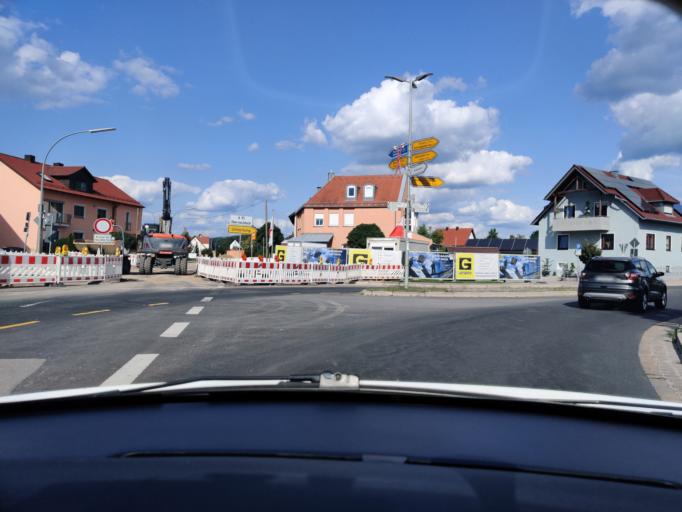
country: DE
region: Bavaria
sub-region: Upper Palatinate
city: Nabburg
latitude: 49.4532
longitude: 12.1865
